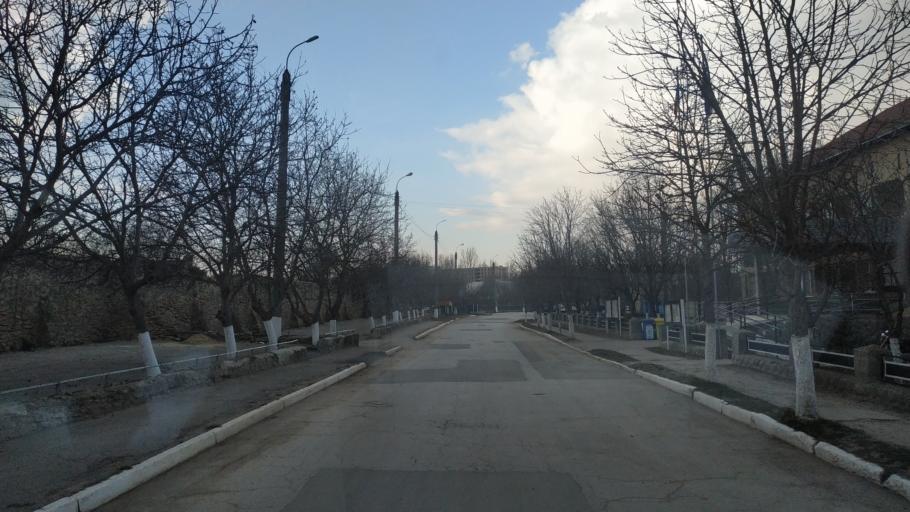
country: MD
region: Anenii Noi
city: Anenii Noi
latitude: 47.0068
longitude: 29.2960
